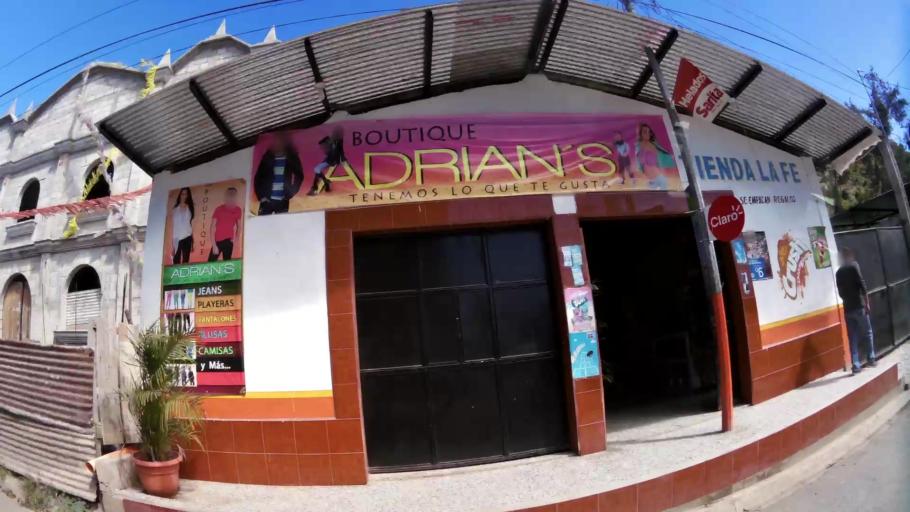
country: GT
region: Solola
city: Panajachel
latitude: 14.7382
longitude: -91.1502
